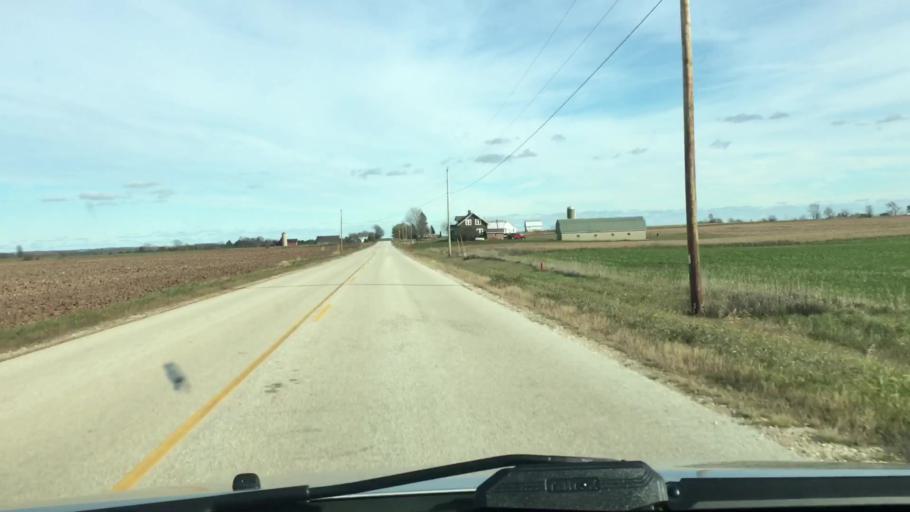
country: US
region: Wisconsin
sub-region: Kewaunee County
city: Algoma
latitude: 44.6974
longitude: -87.5966
